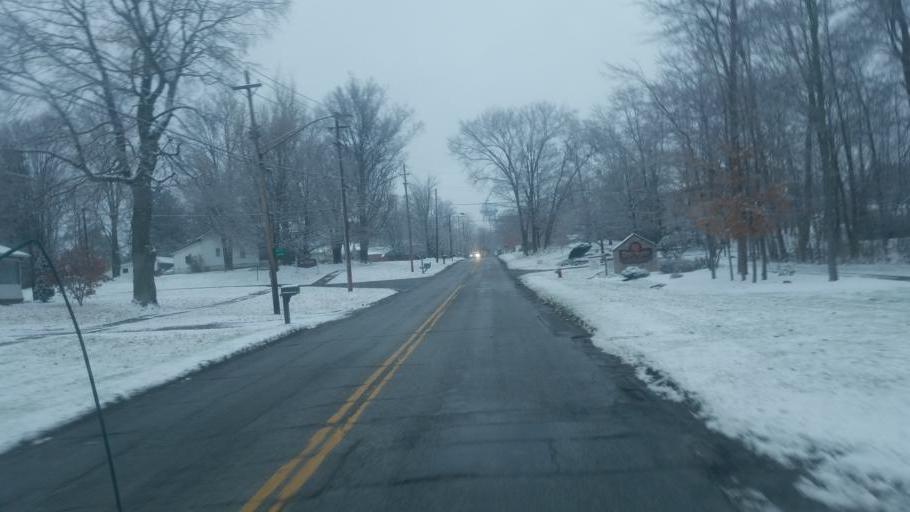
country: US
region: Ohio
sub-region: Geauga County
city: Burton
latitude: 41.4680
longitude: -81.1451
